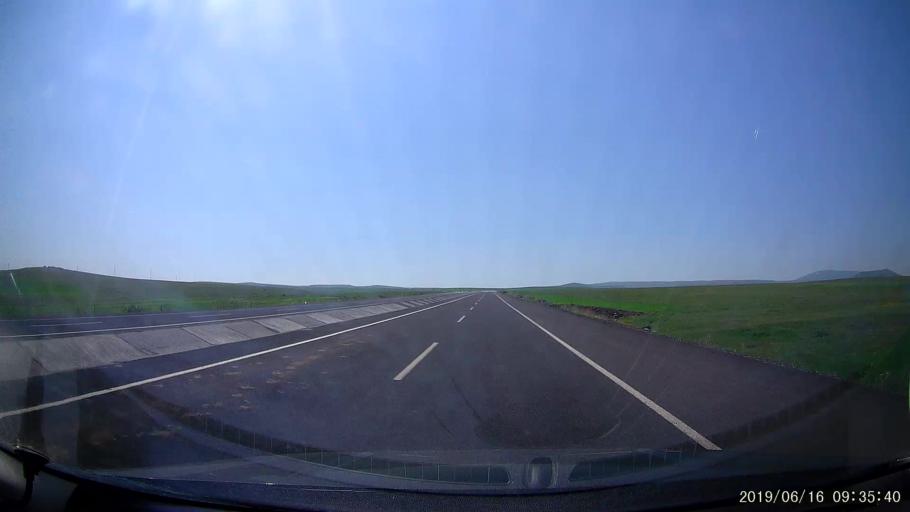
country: TR
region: Kars
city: Kars
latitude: 40.5683
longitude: 43.1597
